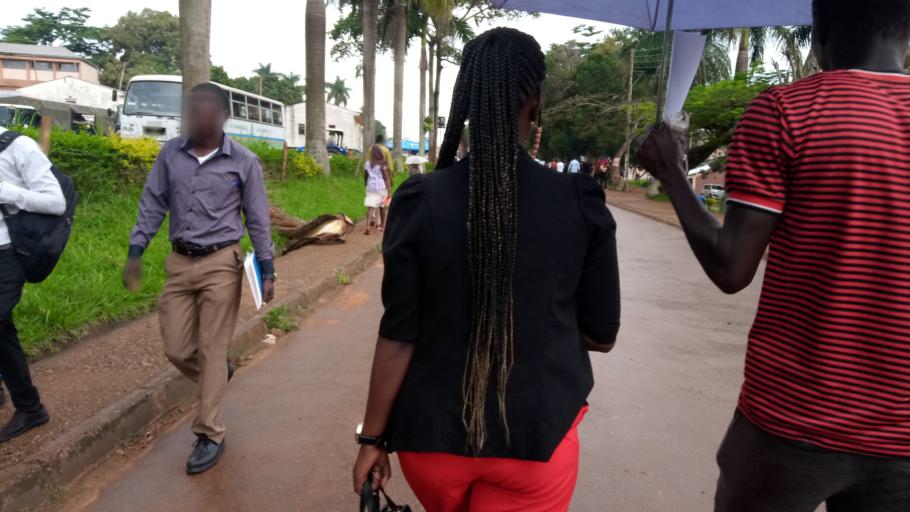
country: UG
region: Central Region
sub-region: Wakiso District
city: Kireka
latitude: 0.3477
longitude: 32.6303
